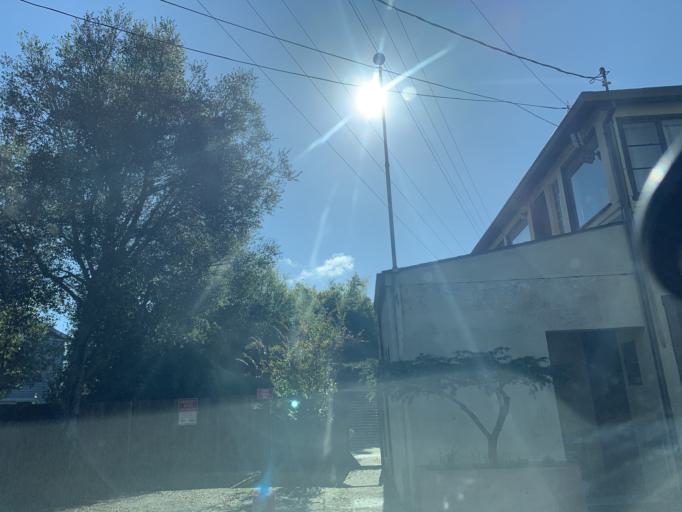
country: US
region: California
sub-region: Marin County
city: Strawberry
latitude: 37.9063
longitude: -122.5179
